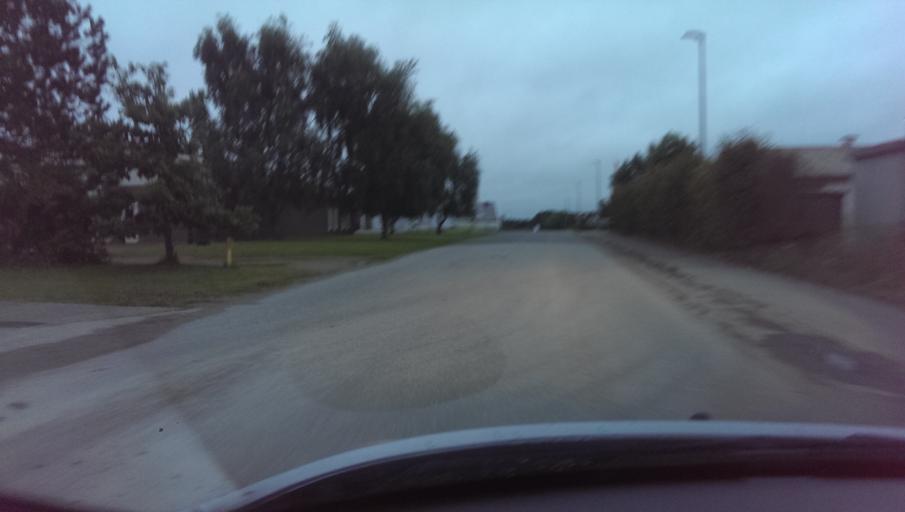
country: DK
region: South Denmark
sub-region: Varde Kommune
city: Olgod
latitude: 55.8146
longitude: 8.6366
